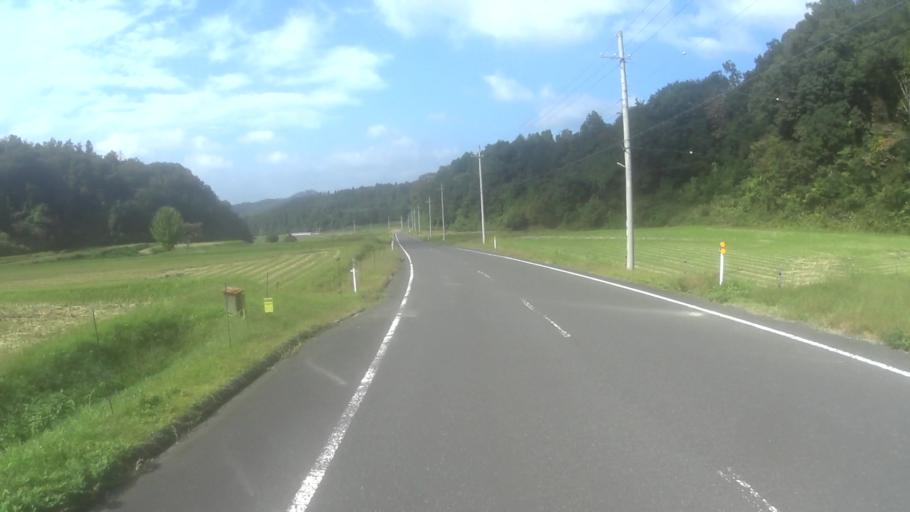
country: JP
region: Kyoto
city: Miyazu
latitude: 35.6020
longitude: 135.1521
